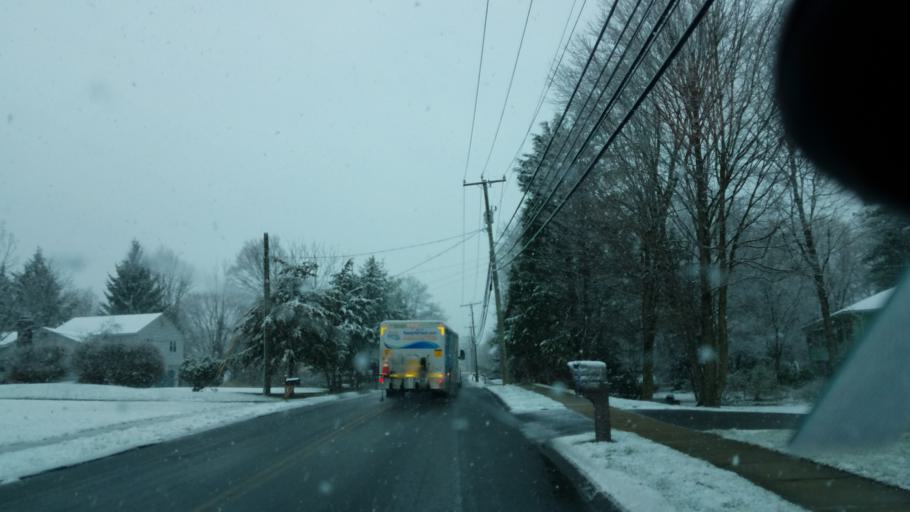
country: US
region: Connecticut
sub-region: New Haven County
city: Cheshire
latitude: 41.4850
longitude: -72.9087
